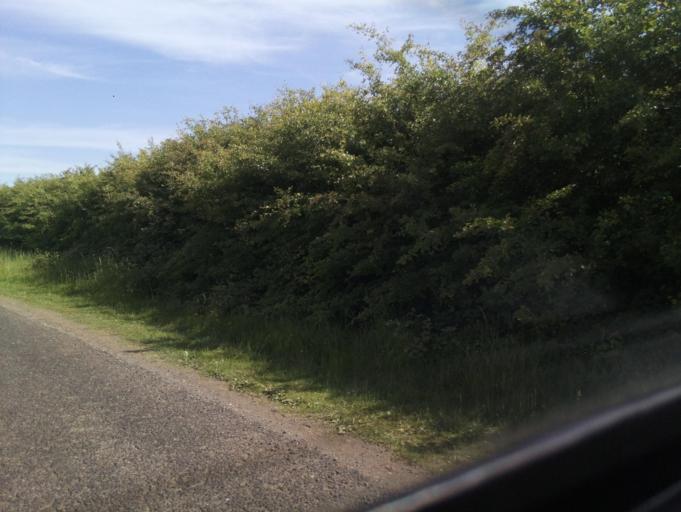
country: GB
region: England
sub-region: Lincolnshire
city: Skellingthorpe
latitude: 53.1703
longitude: -0.6424
